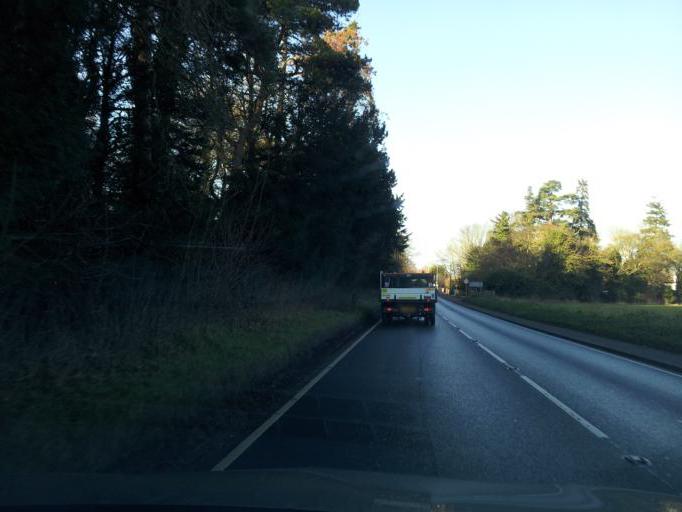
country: GB
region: England
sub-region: Suffolk
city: Bury St Edmunds
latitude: 52.2277
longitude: 0.7325
